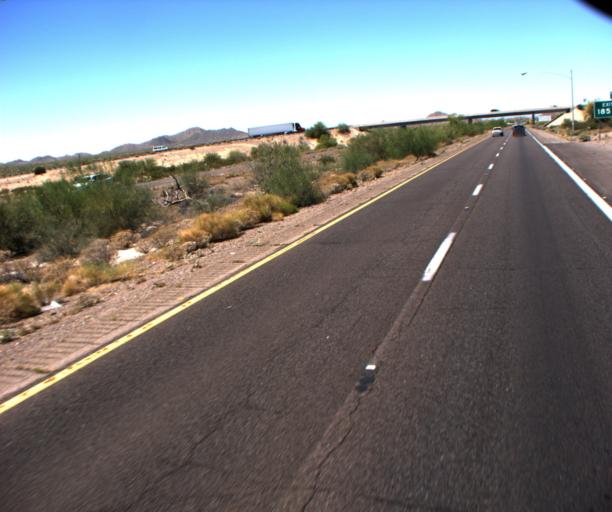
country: US
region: Arizona
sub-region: Pinal County
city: Sacaton
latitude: 33.0013
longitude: -111.7513
